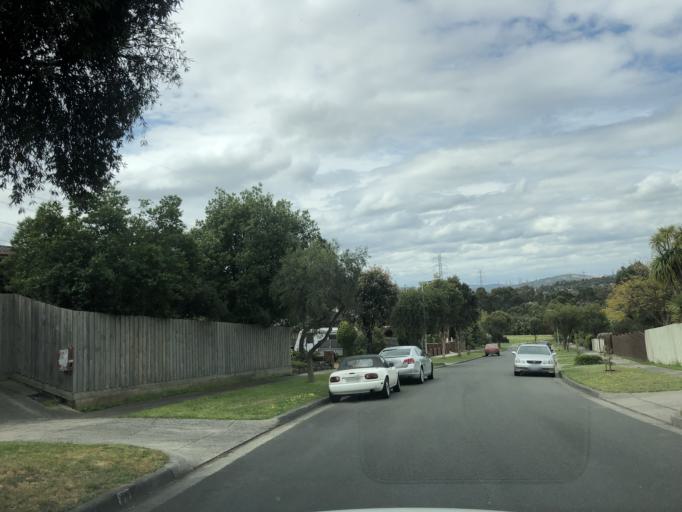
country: AU
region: Victoria
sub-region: Monash
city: Mulgrave
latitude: -37.9324
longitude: 145.2046
